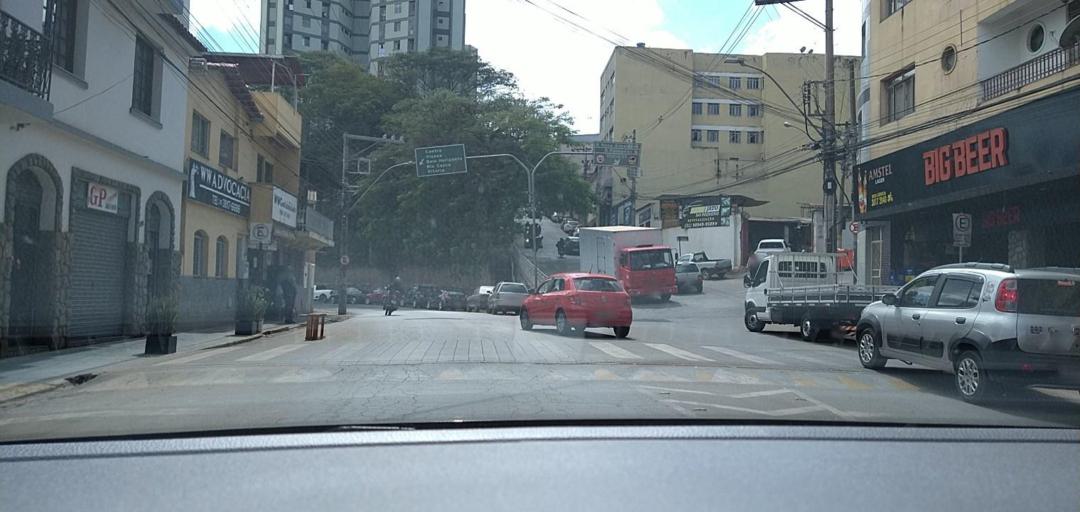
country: BR
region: Minas Gerais
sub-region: Ponte Nova
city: Ponte Nova
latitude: -20.4143
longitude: -42.8990
